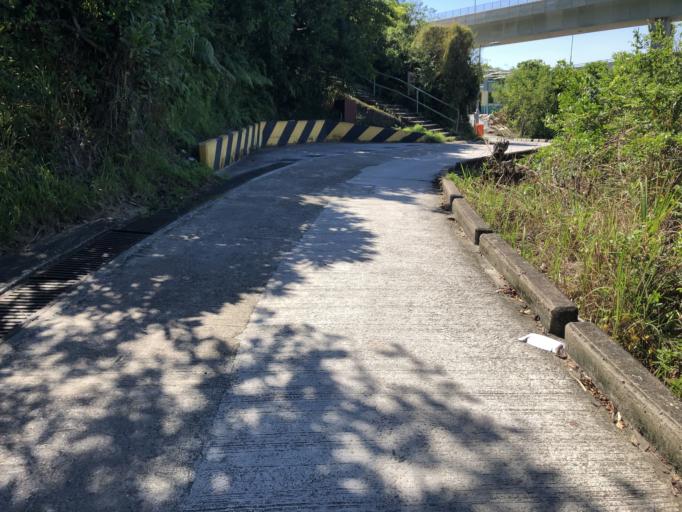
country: HK
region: Tuen Mun
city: Tuen Mun
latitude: 22.2975
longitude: 113.9681
